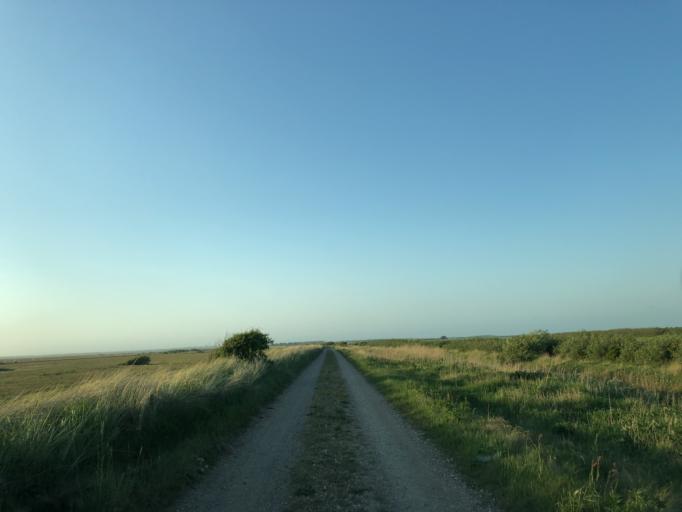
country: DK
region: Central Jutland
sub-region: Ringkobing-Skjern Kommune
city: Ringkobing
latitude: 56.2095
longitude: 8.1623
